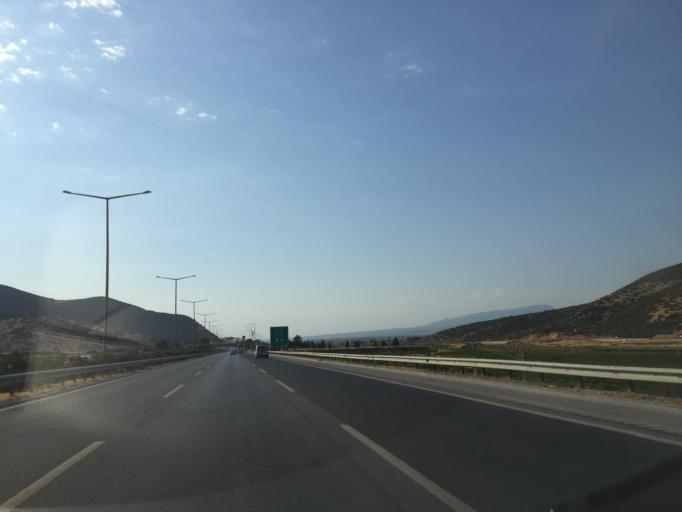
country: TR
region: Izmir
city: Belevi
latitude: 38.0635
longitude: 27.4177
